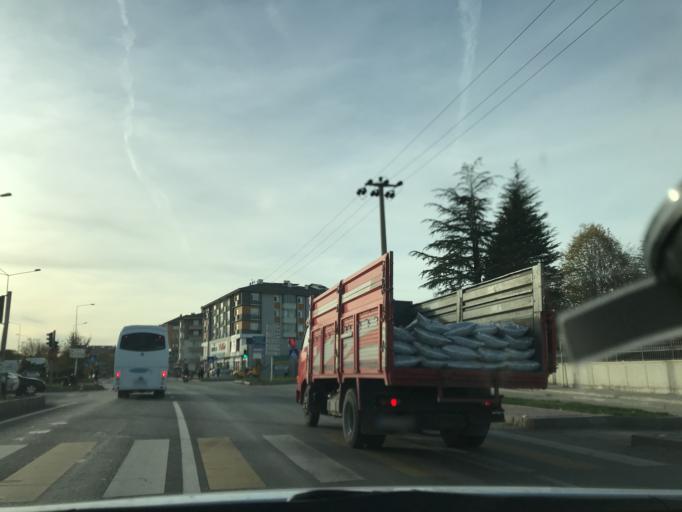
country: TR
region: Bolu
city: Bolu
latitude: 40.7390
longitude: 31.6109
